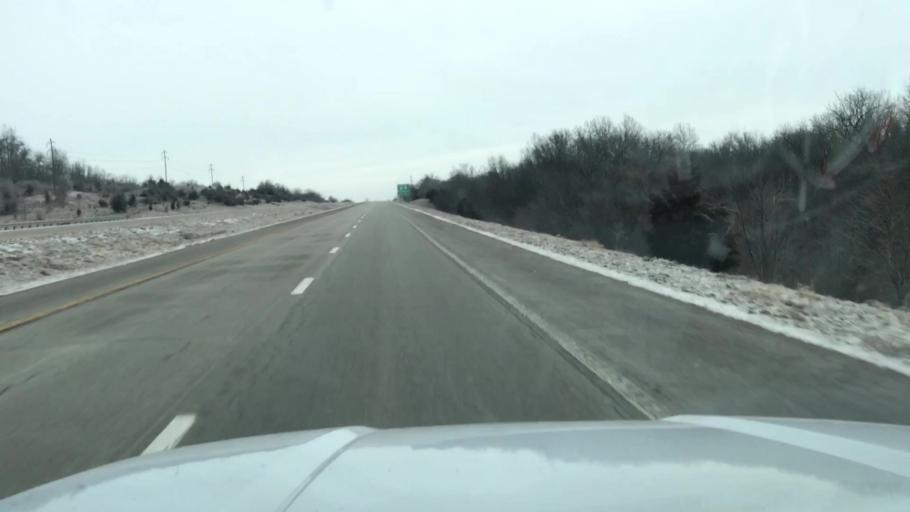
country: US
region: Missouri
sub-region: Andrew County
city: Savannah
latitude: 39.9403
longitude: -94.8600
